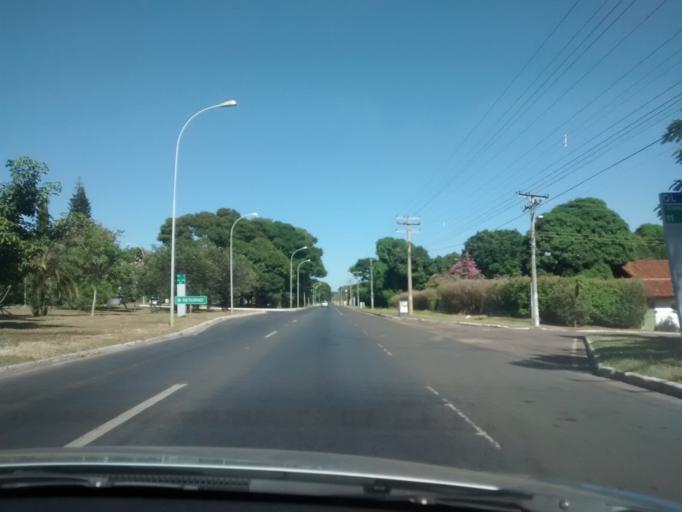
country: BR
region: Federal District
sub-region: Brasilia
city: Brasilia
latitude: -15.8457
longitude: -47.8968
